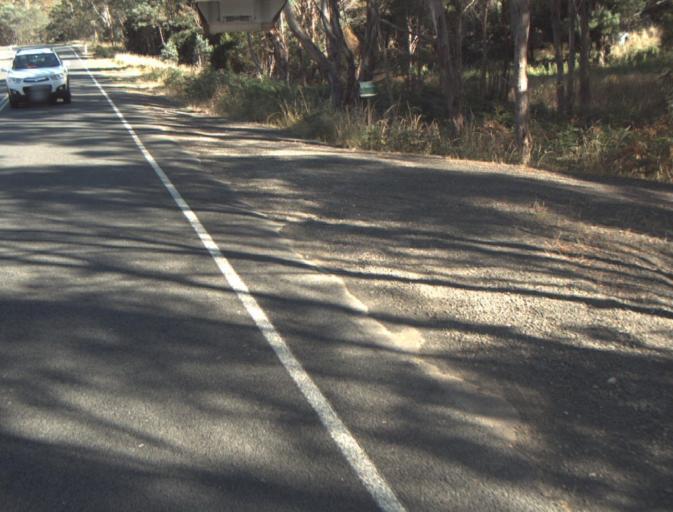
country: AU
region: Tasmania
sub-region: Launceston
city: Newstead
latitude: -41.4189
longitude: 147.2640
